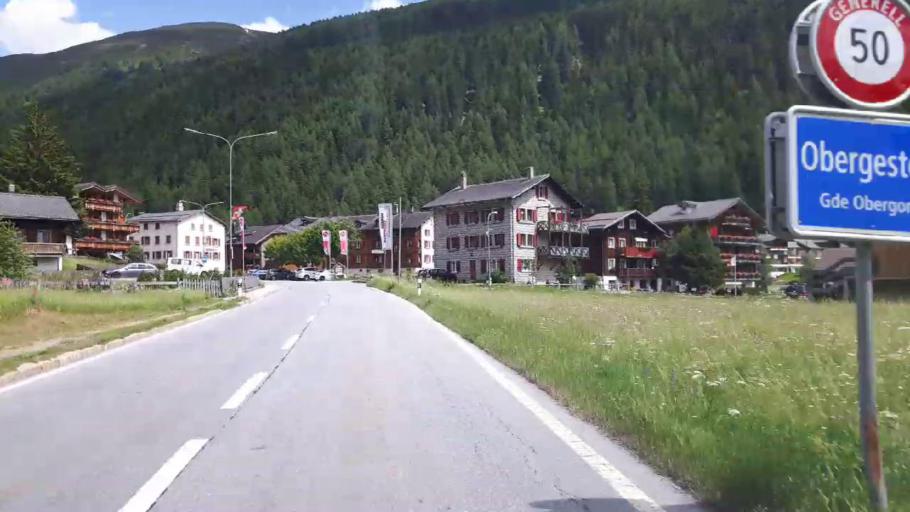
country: IT
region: Piedmont
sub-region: Provincia Verbano-Cusio-Ossola
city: Formazza
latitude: 46.5137
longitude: 8.3225
